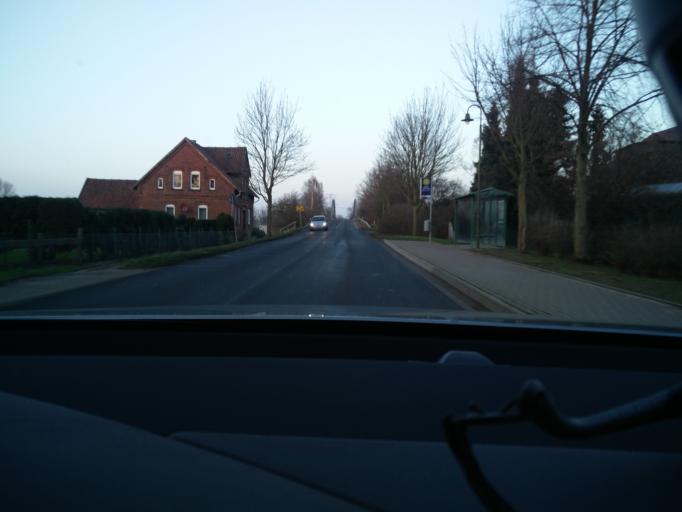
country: DE
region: Lower Saxony
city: Hohenhameln
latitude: 52.3088
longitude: 10.0487
